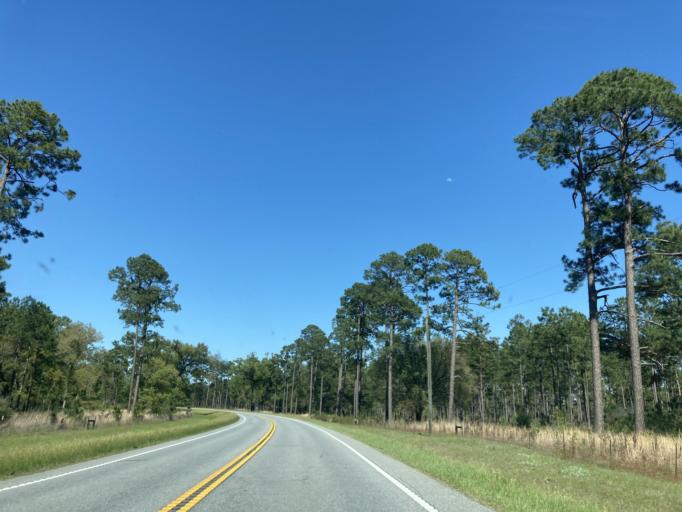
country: US
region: Georgia
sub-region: Baker County
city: Newton
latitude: 31.2135
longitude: -84.4553
